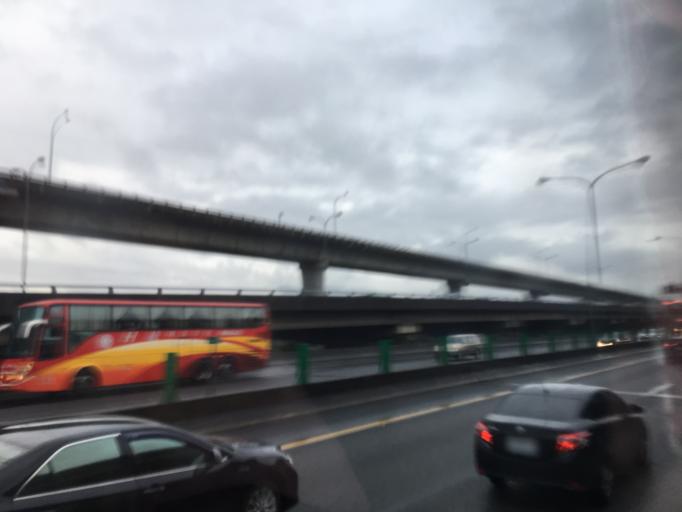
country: TW
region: Taipei
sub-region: Taipei
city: Banqiao
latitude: 25.0703
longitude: 121.4444
